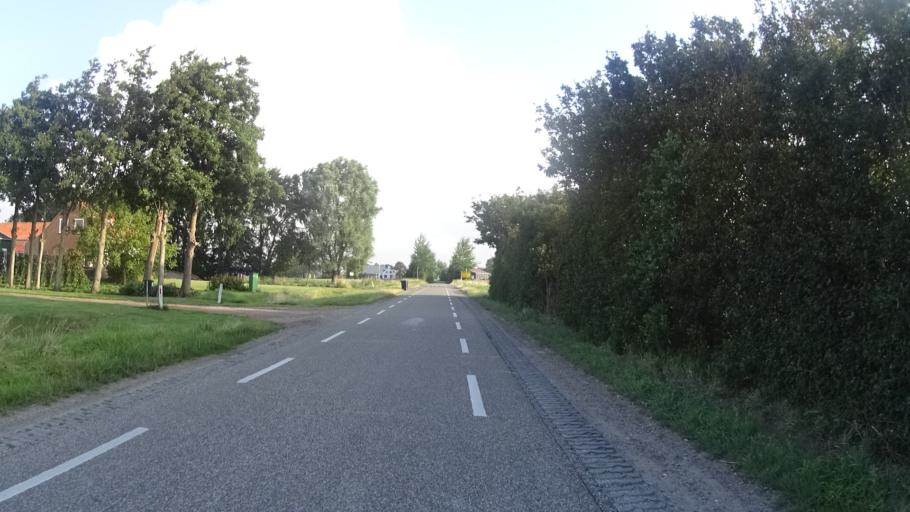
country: NL
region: Zeeland
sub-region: Gemeente Middelburg
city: Middelburg
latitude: 51.5363
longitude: 3.6276
